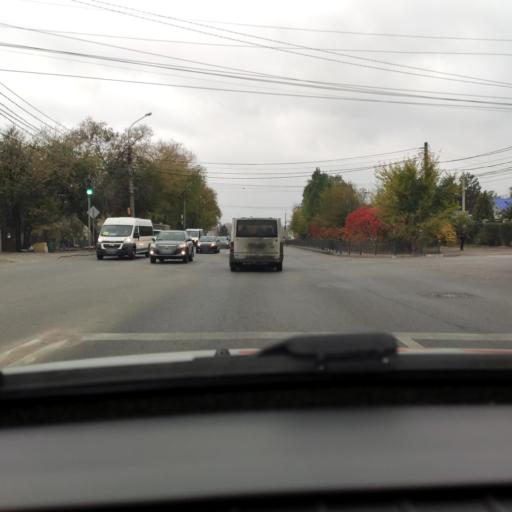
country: RU
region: Voronezj
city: Voronezh
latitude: 51.7006
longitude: 39.2326
